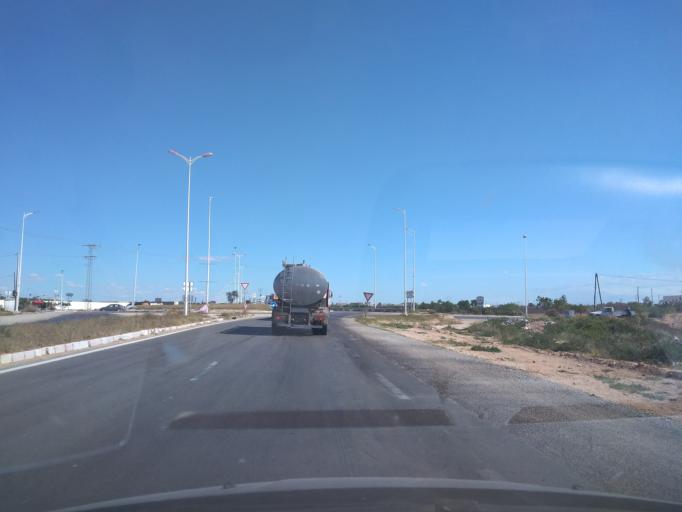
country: TN
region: Safaqis
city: Sfax
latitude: 34.8021
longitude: 10.6883
